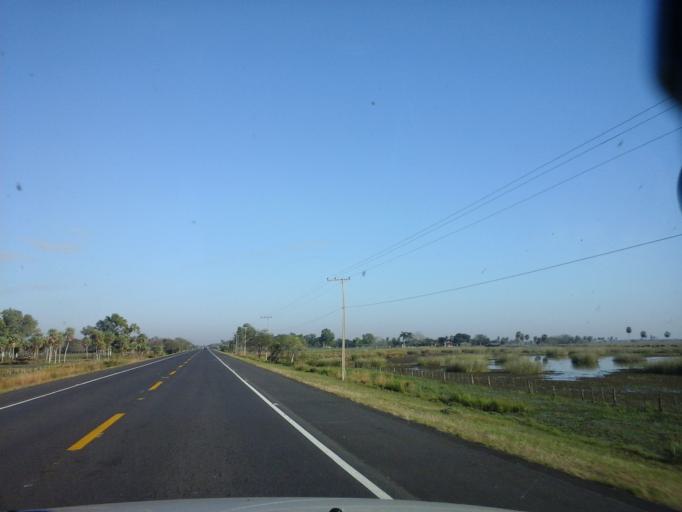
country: PY
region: Neembucu
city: Pilar
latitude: -26.8545
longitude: -58.0380
